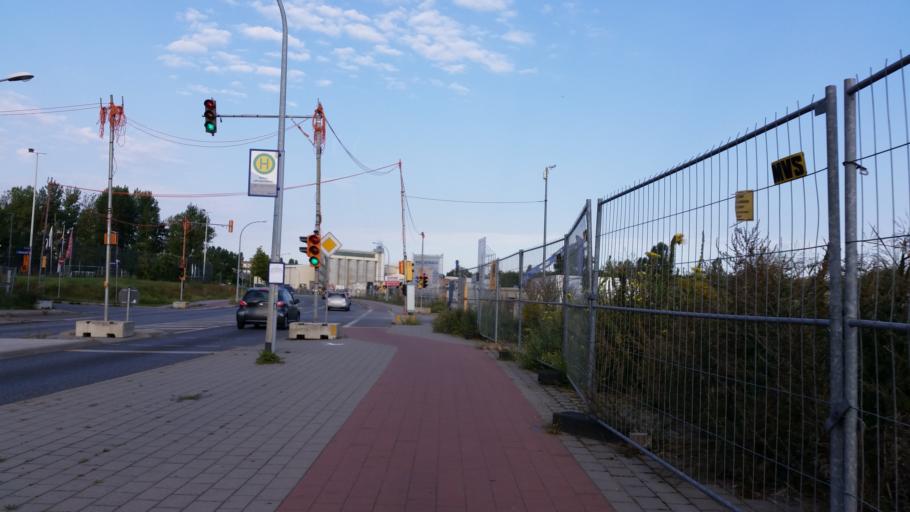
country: DE
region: Brandenburg
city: Teltow
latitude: 52.4048
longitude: 13.2602
